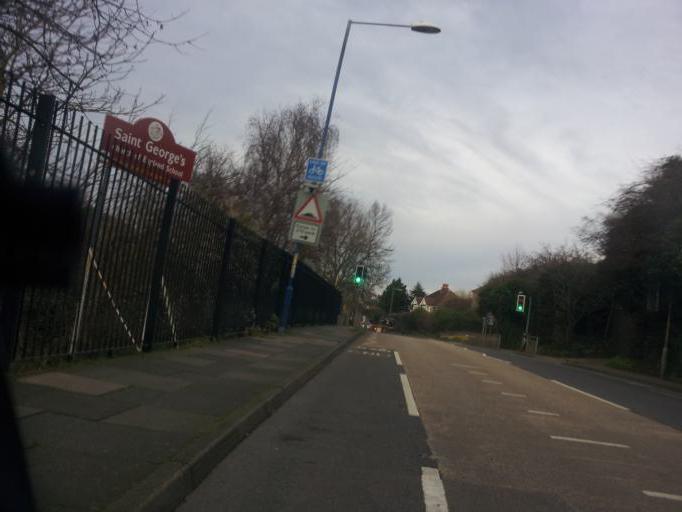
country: GB
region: England
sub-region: Kent
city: Gravesend
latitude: 51.4281
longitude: 0.3638
